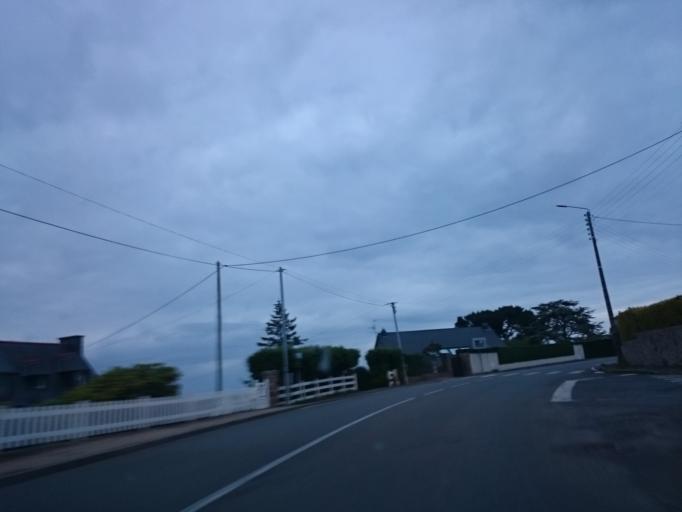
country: FR
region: Brittany
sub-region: Departement des Cotes-d'Armor
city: Perros-Guirec
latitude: 48.8114
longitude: -3.4614
